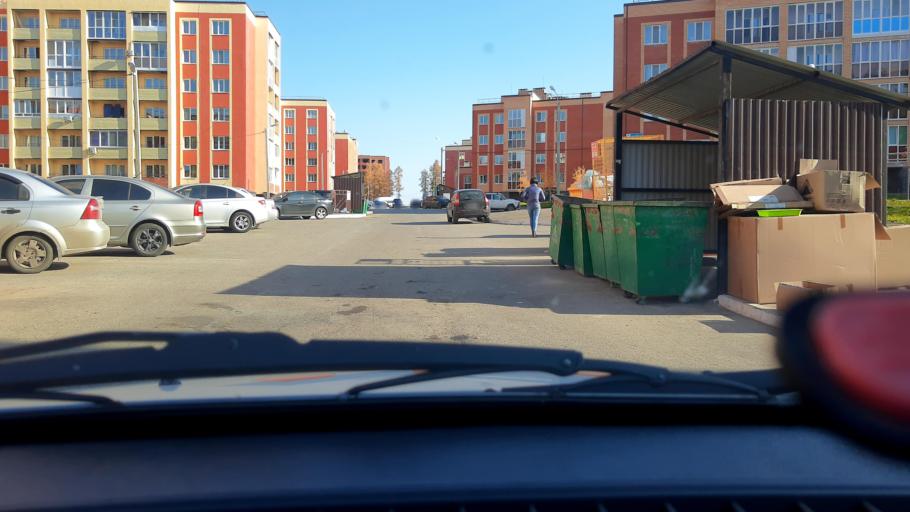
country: RU
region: Bashkortostan
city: Mikhaylovka
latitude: 54.8290
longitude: 55.8615
